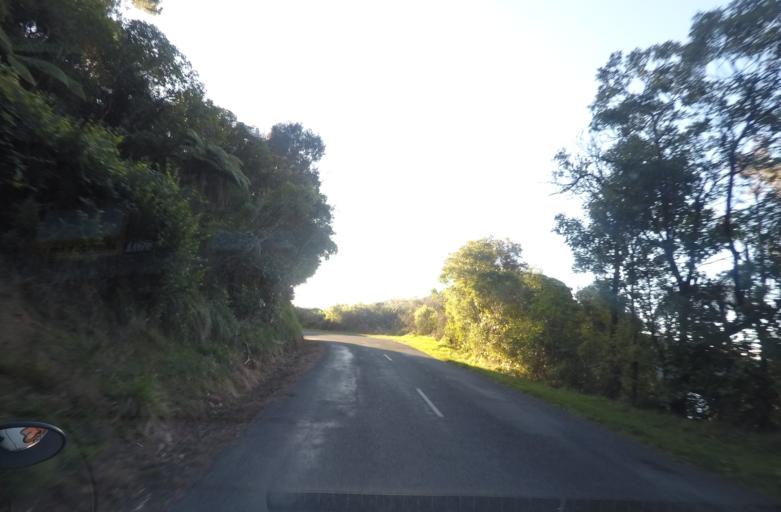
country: NZ
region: Marlborough
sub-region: Marlborough District
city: Picton
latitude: -41.2705
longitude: 173.9511
